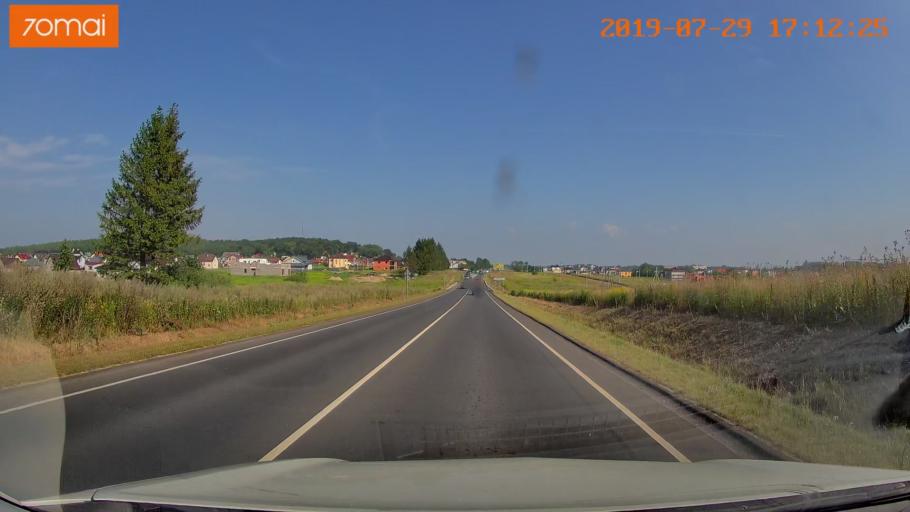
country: RU
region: Kaliningrad
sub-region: Gorod Kaliningrad
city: Kaliningrad
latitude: 54.7885
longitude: 20.3971
